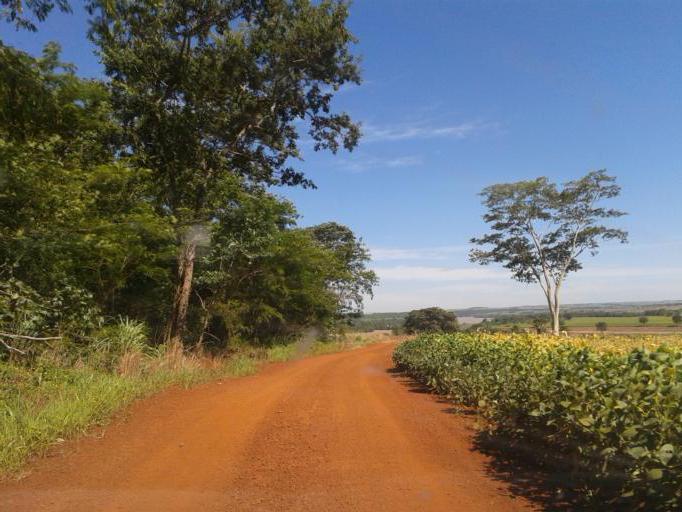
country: BR
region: Minas Gerais
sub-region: Capinopolis
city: Capinopolis
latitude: -18.6119
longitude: -49.6137
